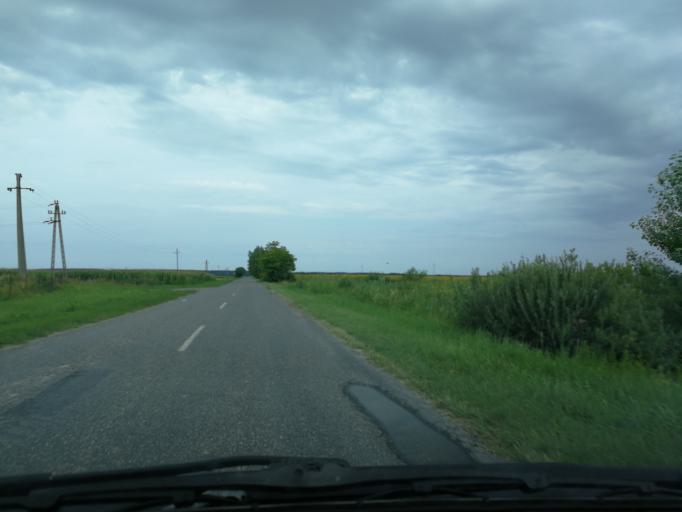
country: HU
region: Bacs-Kiskun
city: Batya
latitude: 46.4488
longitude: 18.9761
